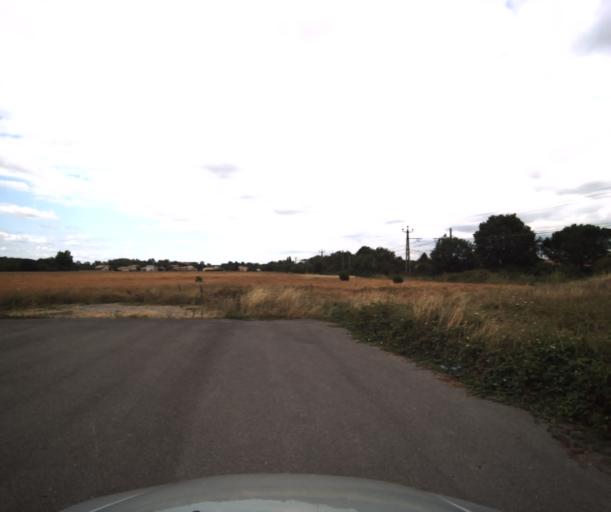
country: FR
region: Midi-Pyrenees
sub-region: Departement de la Haute-Garonne
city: Muret
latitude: 43.4512
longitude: 1.3133
